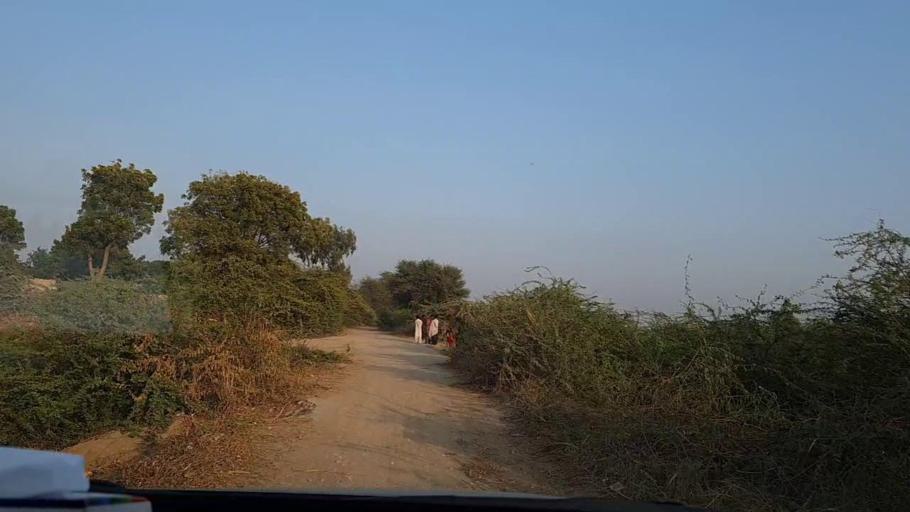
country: PK
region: Sindh
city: Tando Ghulam Ali
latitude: 25.1881
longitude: 68.9095
